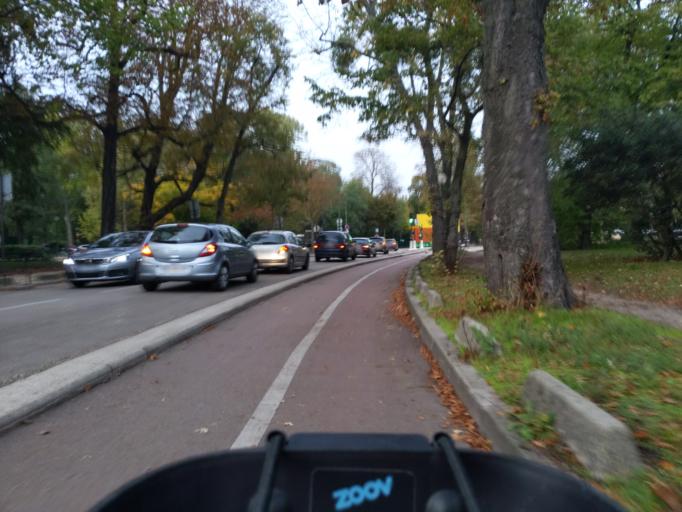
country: FR
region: Ile-de-France
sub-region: Departement des Hauts-de-Seine
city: Boulogne-Billancourt
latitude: 48.8572
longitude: 2.2627
